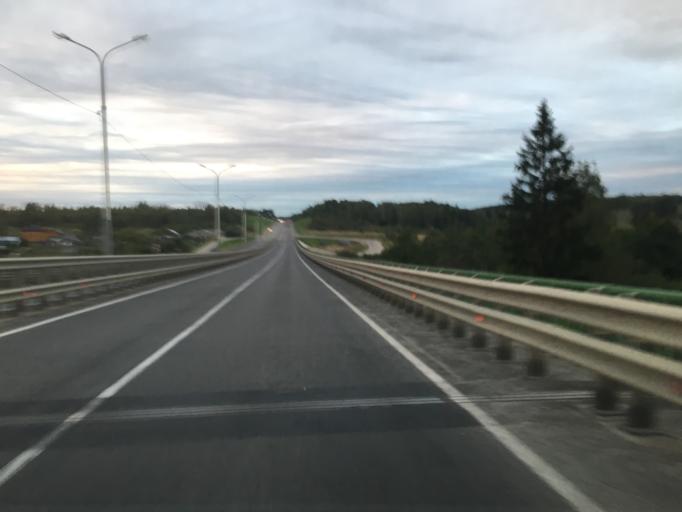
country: RU
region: Kaluga
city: Kaluga
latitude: 54.5985
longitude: 36.3218
